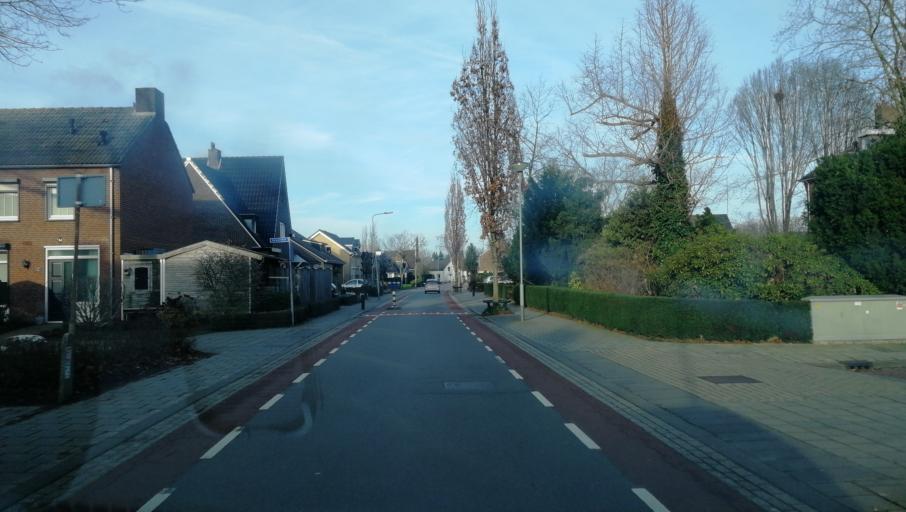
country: NL
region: Limburg
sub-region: Gemeente Venlo
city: Tegelen
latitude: 51.3350
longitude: 6.0982
